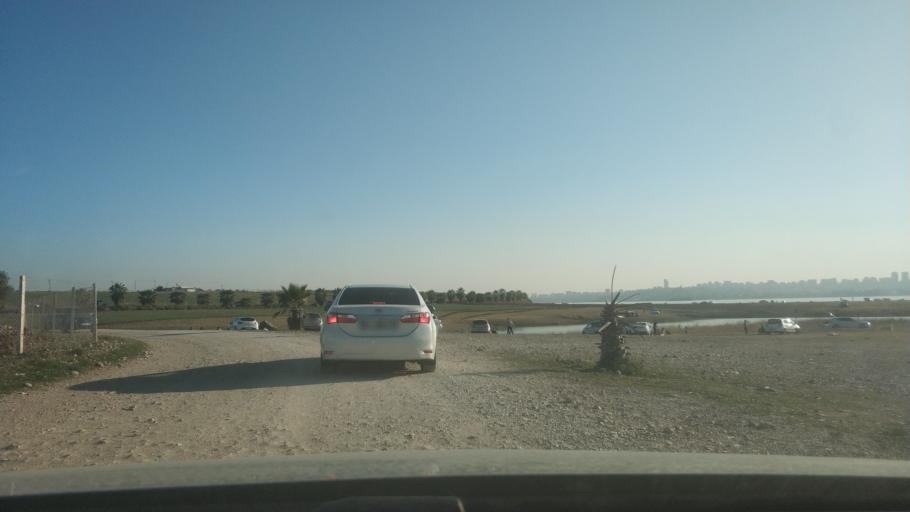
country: TR
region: Adana
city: Adana
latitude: 37.0943
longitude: 35.3001
